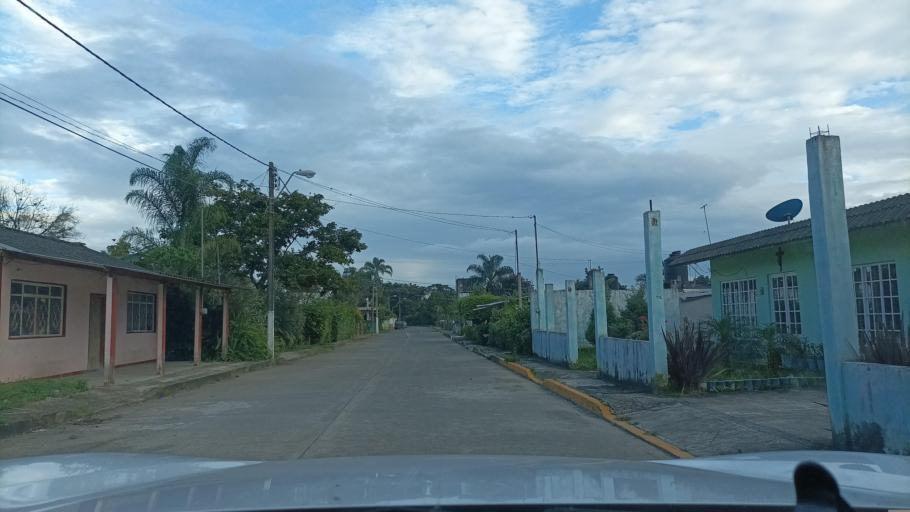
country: MX
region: Veracruz
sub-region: Ixtaczoquitlan
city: Buenavista
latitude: 18.9113
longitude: -97.0569
